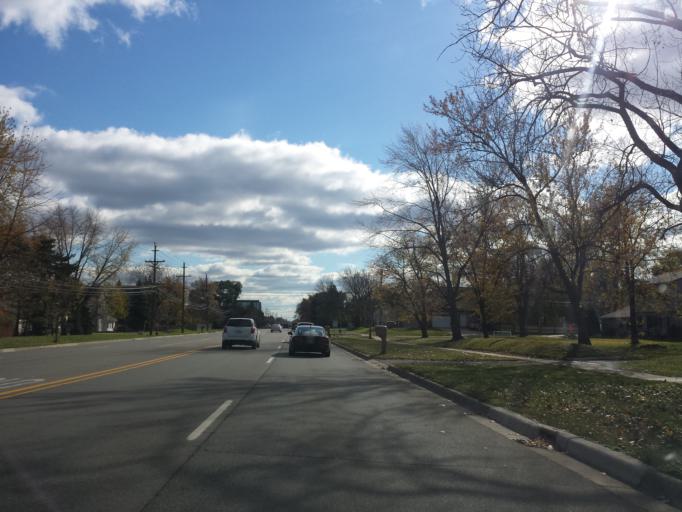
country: US
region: Michigan
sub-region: Oakland County
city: Troy
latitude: 42.5703
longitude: -83.1677
